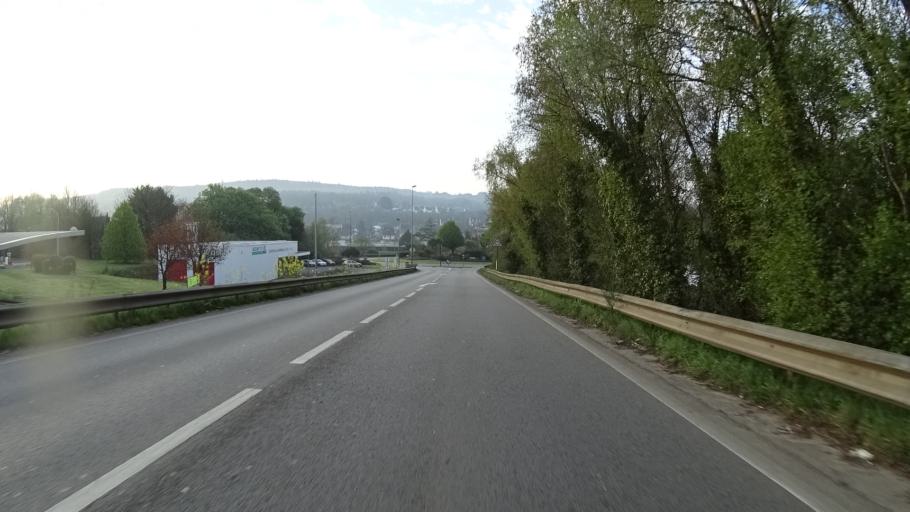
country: FR
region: Brittany
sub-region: Departement du Finistere
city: Landerneau
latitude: 48.4484
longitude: -4.2639
